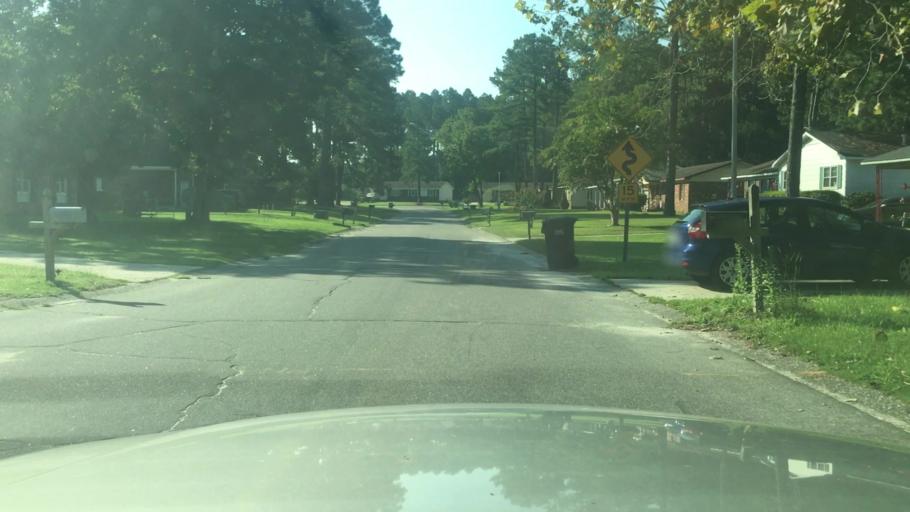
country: US
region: North Carolina
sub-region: Cumberland County
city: Spring Lake
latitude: 35.1565
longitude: -78.9121
